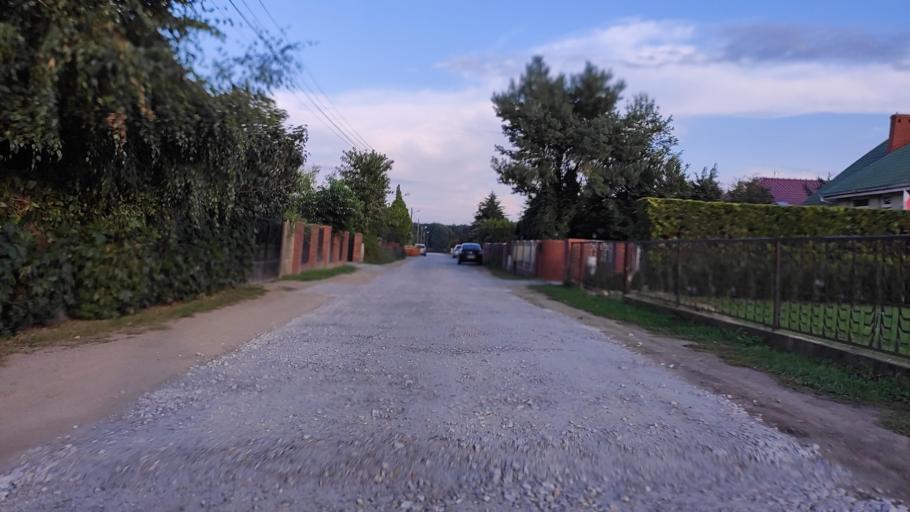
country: PL
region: Greater Poland Voivodeship
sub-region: Powiat poznanski
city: Kostrzyn
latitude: 52.4018
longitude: 17.1685
